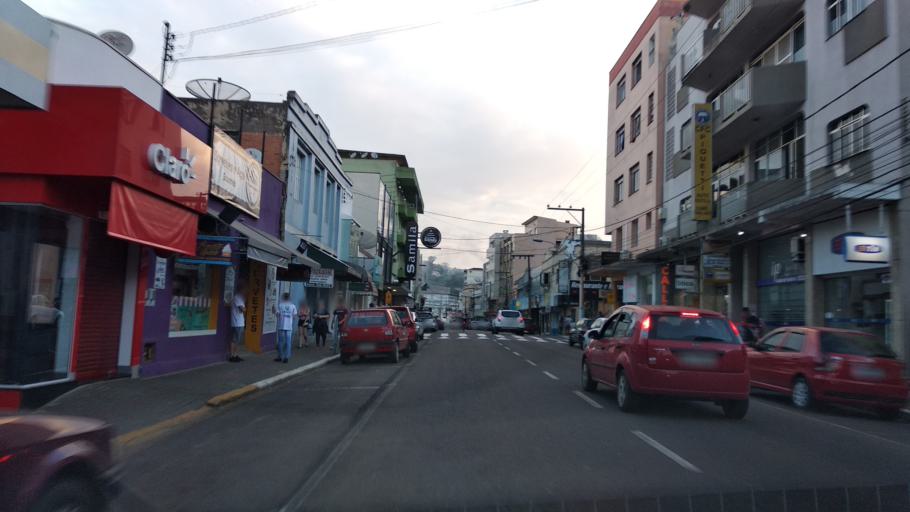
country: BR
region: Santa Catarina
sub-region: Videira
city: Videira
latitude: -27.0038
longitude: -51.1569
